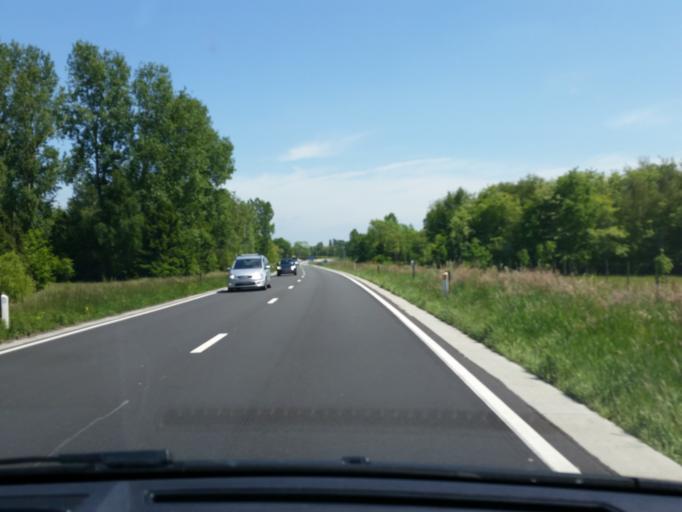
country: BE
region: Flanders
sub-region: Provincie Antwerpen
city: Sint-Katelijne-Waver
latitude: 51.0491
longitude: 4.5259
